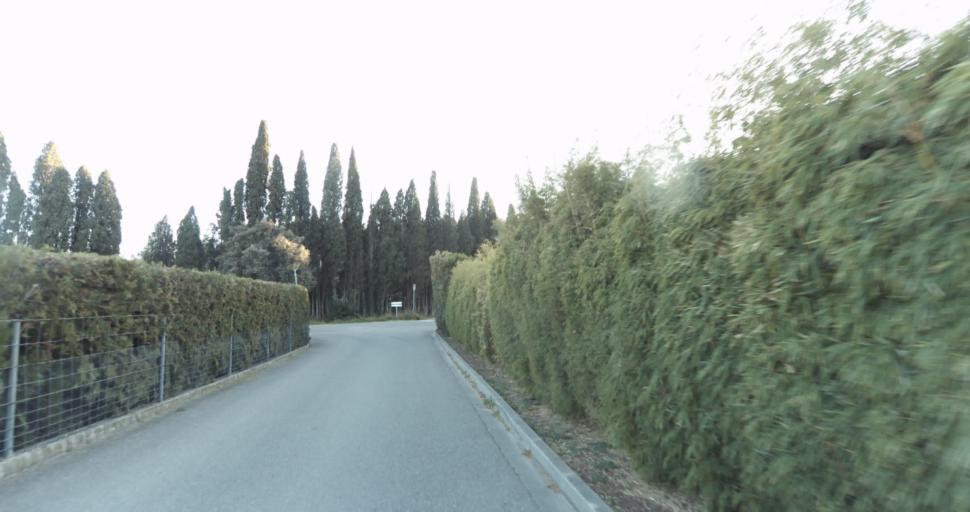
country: FR
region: Provence-Alpes-Cote d'Azur
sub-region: Departement des Bouches-du-Rhone
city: Barbentane
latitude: 43.8840
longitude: 4.7648
